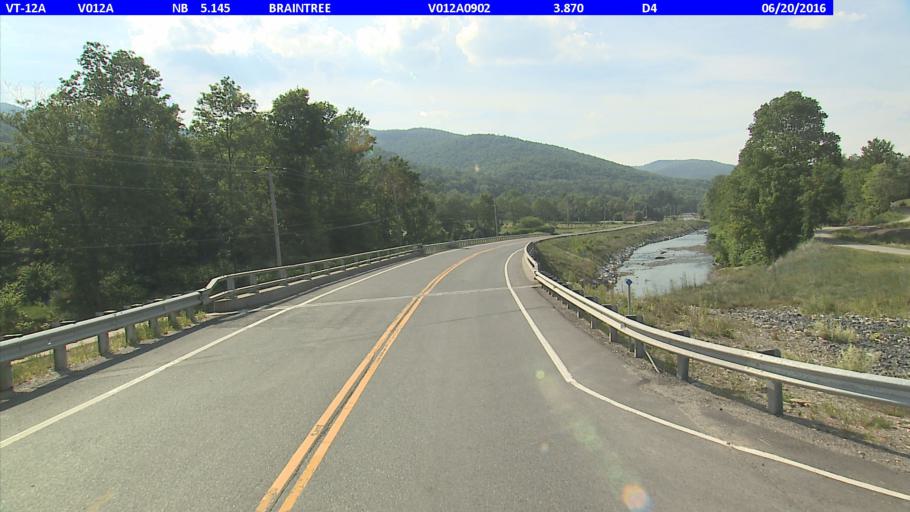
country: US
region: Vermont
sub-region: Orange County
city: Randolph
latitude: 43.9650
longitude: -72.7417
